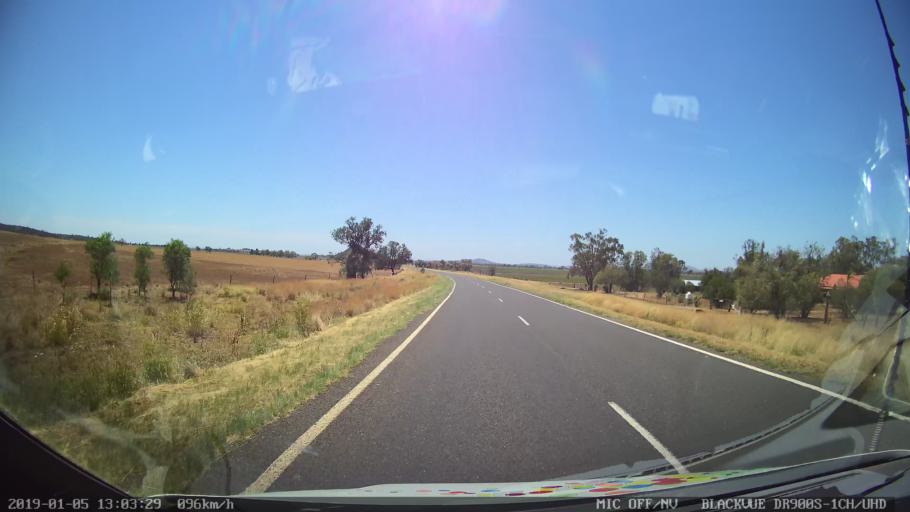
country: AU
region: New South Wales
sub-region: Gunnedah
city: Gunnedah
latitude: -31.1105
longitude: 149.8281
